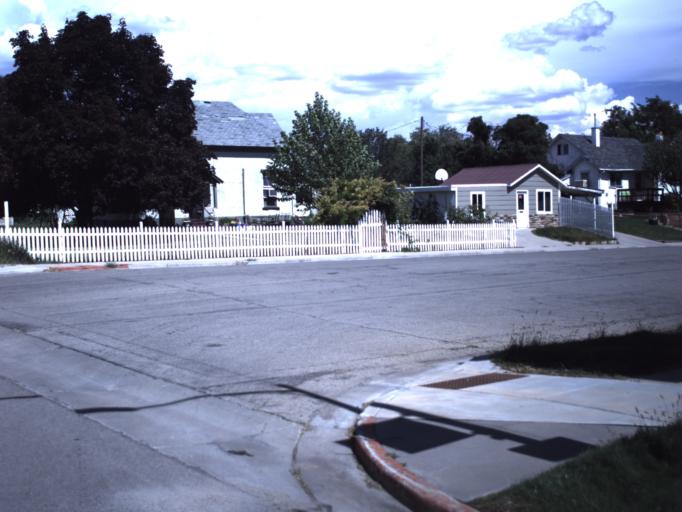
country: US
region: Utah
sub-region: San Juan County
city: Blanding
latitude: 37.6209
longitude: -109.4780
